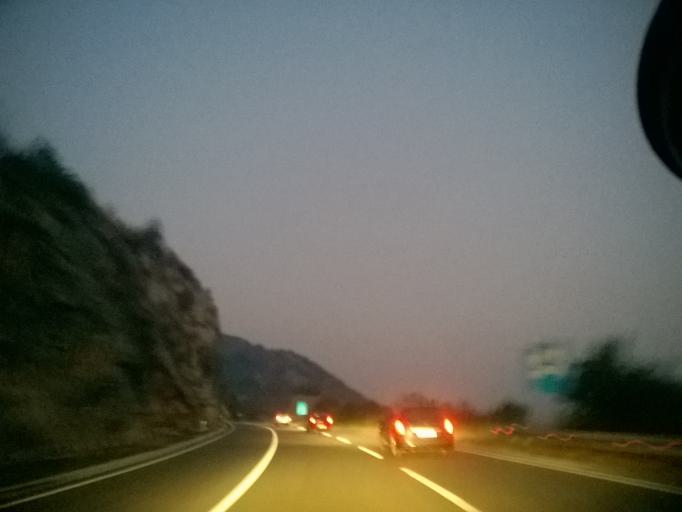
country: ME
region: Cetinje
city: Cetinje
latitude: 42.3810
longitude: 19.0160
